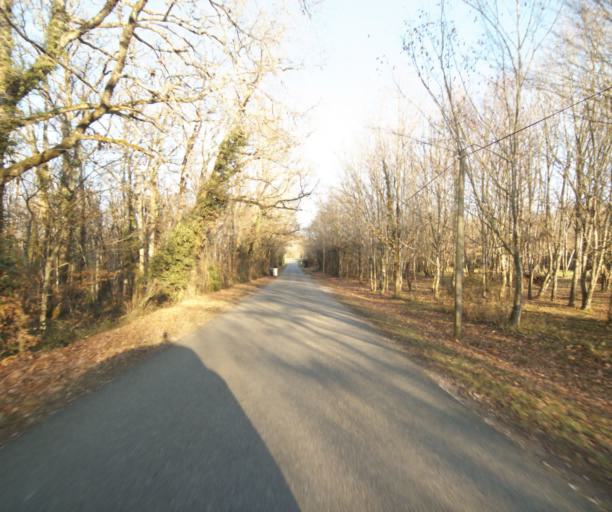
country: FR
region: Midi-Pyrenees
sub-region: Departement du Tarn-et-Garonne
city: Moissac
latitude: 44.1541
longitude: 1.1338
